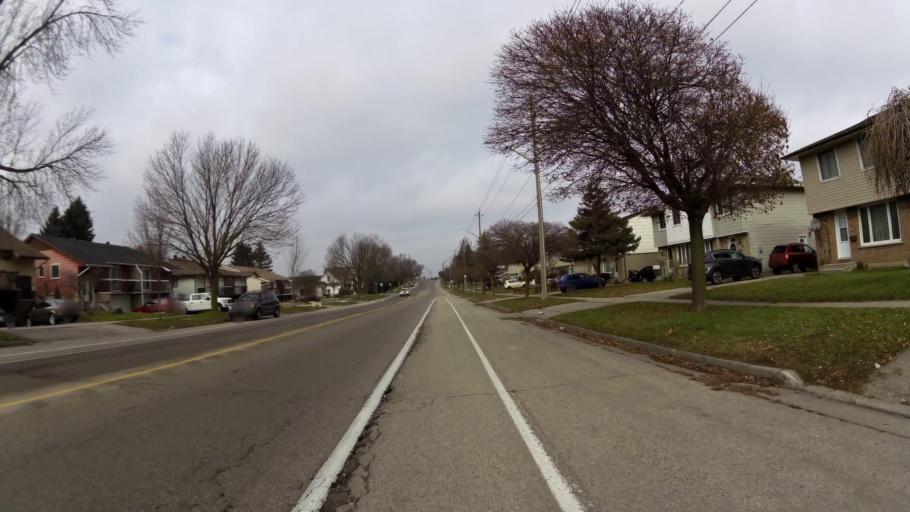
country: CA
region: Ontario
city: Kitchener
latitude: 43.4201
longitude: -80.4845
